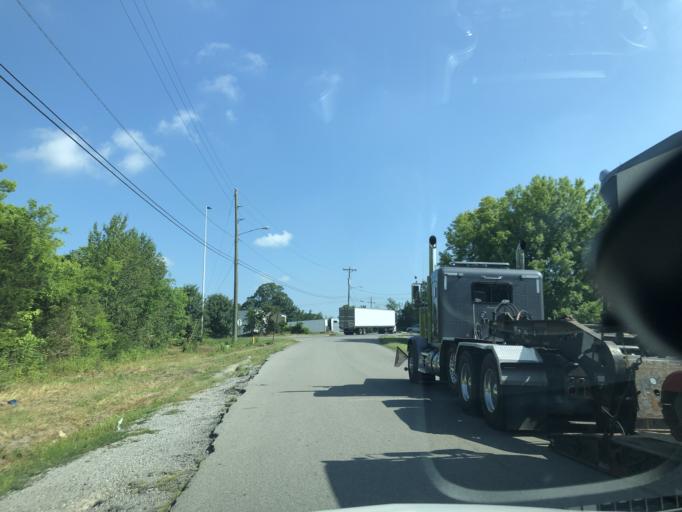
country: US
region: Tennessee
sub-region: Rutherford County
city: La Vergne
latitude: 36.0147
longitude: -86.6161
